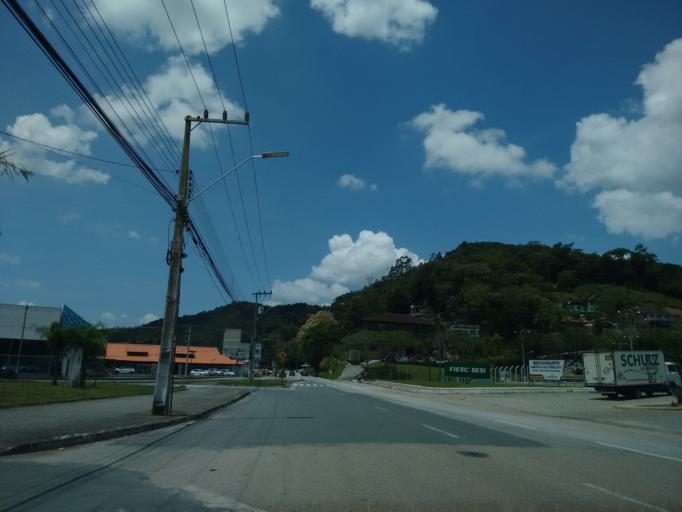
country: BR
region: Santa Catarina
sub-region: Blumenau
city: Blumenau
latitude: -26.9075
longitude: -49.0338
